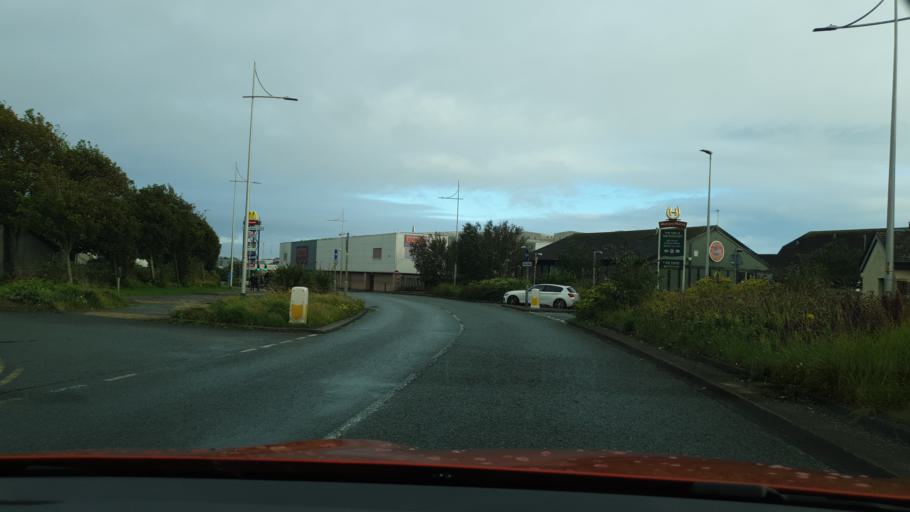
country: GB
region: England
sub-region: Cumbria
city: Barrow in Furness
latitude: 54.1163
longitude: -3.2385
